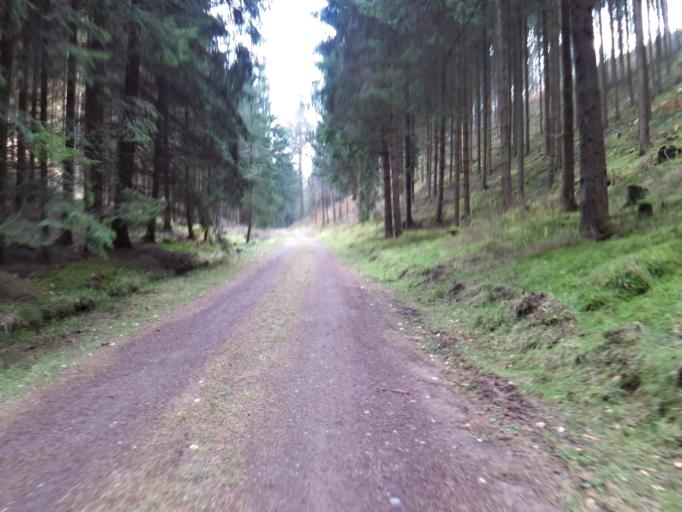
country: DE
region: Rheinland-Pfalz
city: Carlsberg
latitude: 49.4797
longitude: 7.9998
